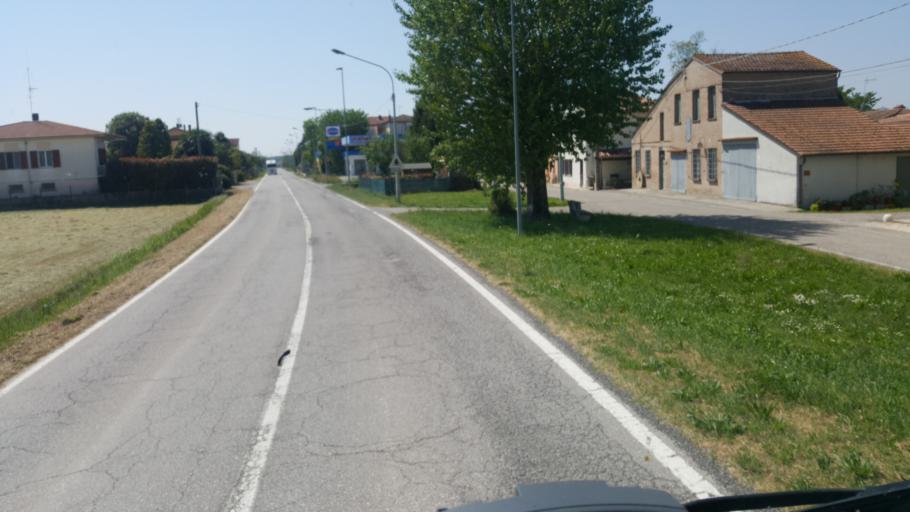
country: IT
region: Veneto
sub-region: Provincia di Rovigo
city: Melara
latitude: 45.0472
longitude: 11.1825
